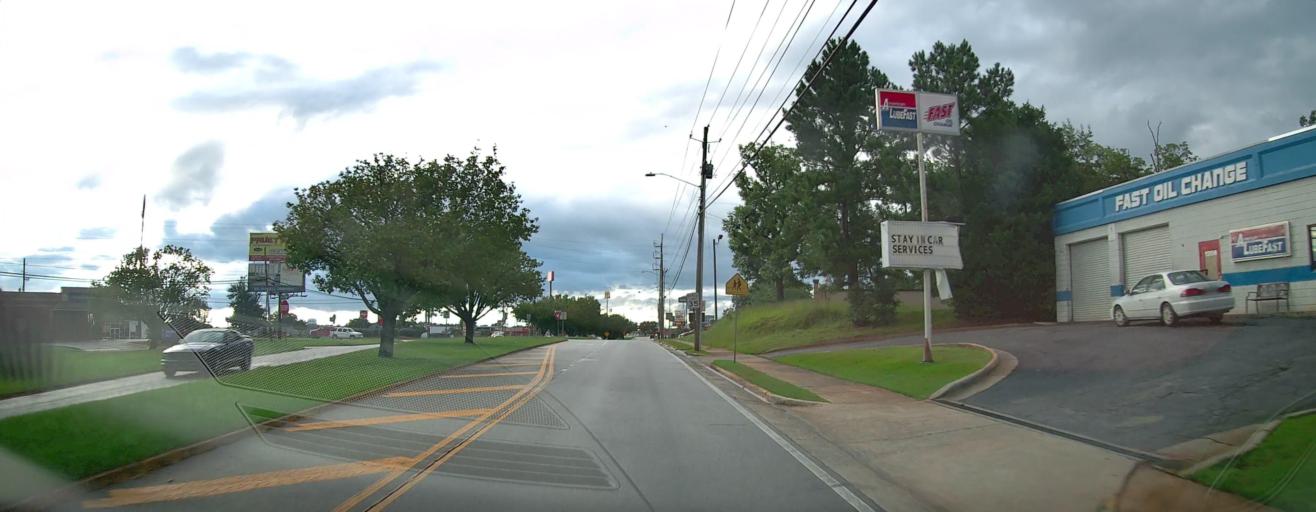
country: US
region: Georgia
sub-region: Houston County
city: Perry
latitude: 32.4654
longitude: -83.7370
